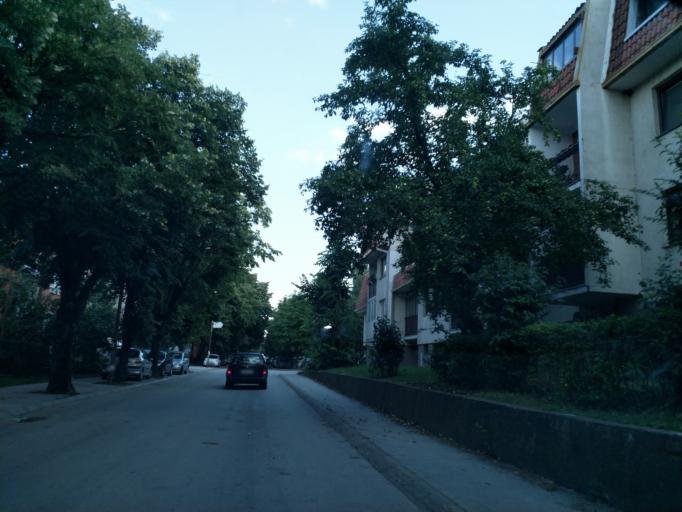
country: RS
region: Central Serbia
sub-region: Pomoravski Okrug
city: Jagodina
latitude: 43.9795
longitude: 21.2467
